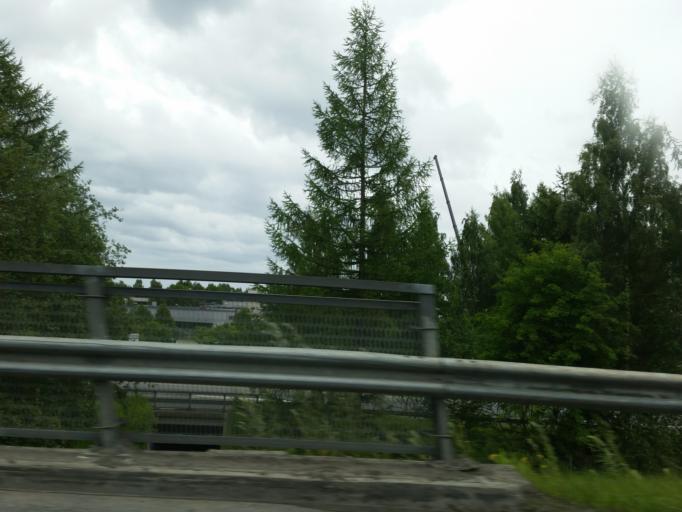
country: FI
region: Northern Savo
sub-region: Kuopio
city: Kuopio
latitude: 62.8995
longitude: 27.6570
